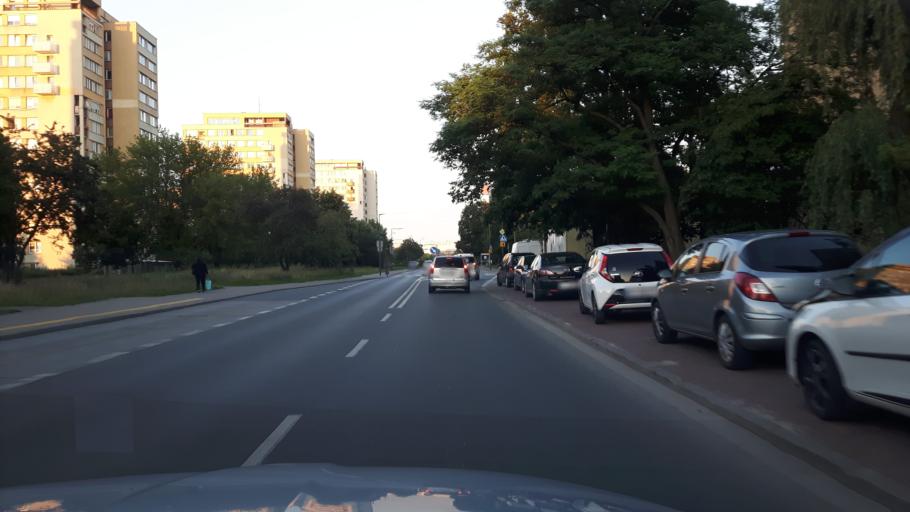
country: PL
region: Masovian Voivodeship
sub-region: Warszawa
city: Mokotow
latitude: 52.1932
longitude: 21.0620
